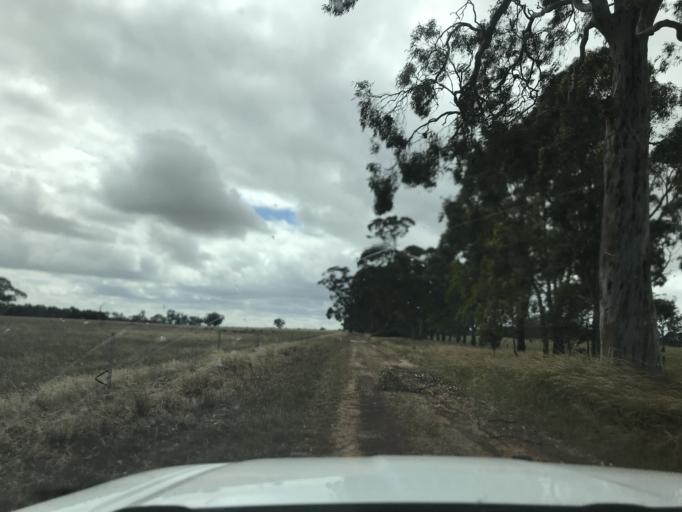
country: AU
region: South Australia
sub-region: Naracoorte and Lucindale
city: Naracoorte
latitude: -36.9009
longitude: 141.4063
